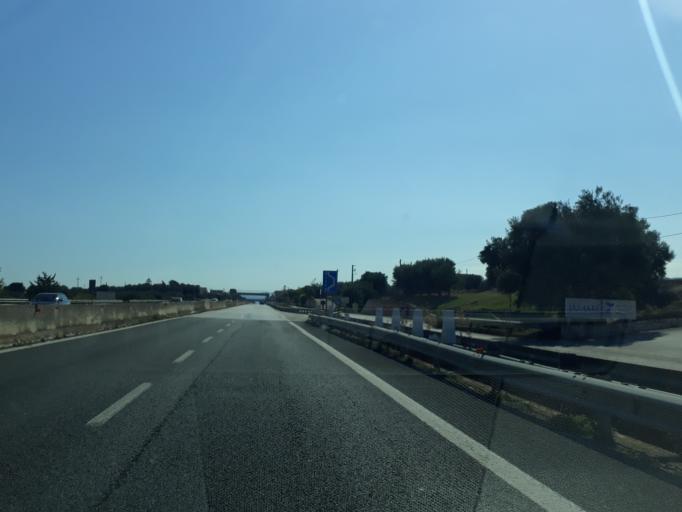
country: IT
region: Apulia
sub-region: Provincia di Brindisi
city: Fasano
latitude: 40.8888
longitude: 17.3337
